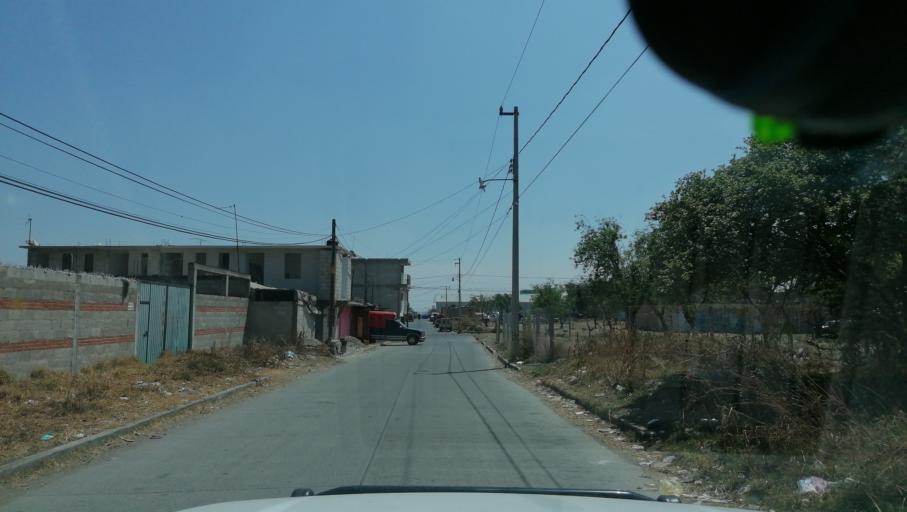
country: MX
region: Puebla
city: Huejotzingo
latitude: 19.1580
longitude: -98.4150
